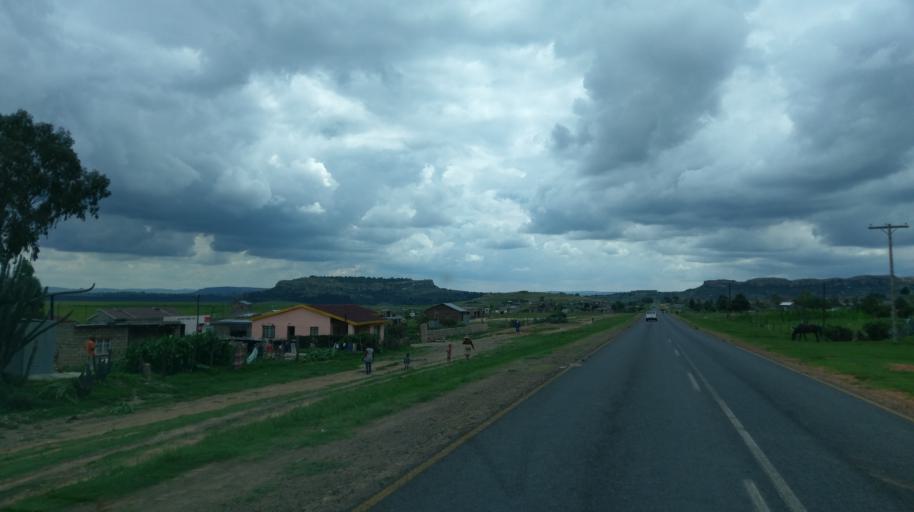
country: LS
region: Berea
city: Teyateyaneng
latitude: -29.0061
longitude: 27.7523
